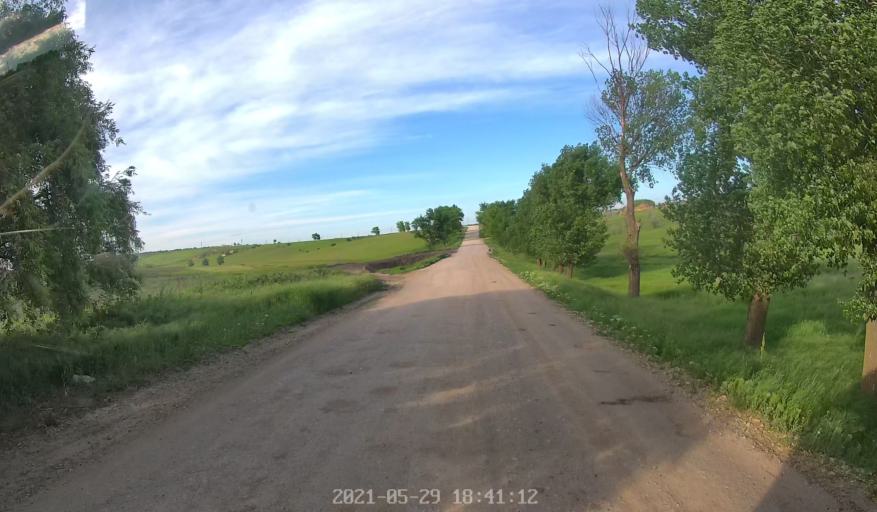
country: MD
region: Chisinau
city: Singera
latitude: 46.8066
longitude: 28.9556
